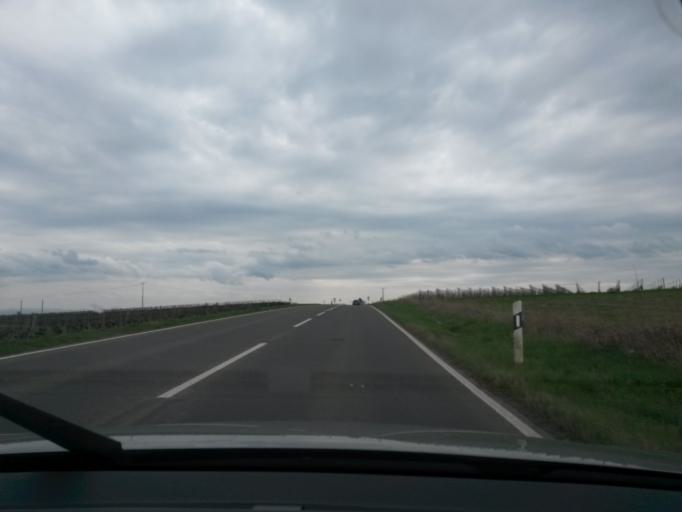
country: DE
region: Rheinland-Pfalz
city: Osthofen
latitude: 49.6671
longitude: 8.3179
